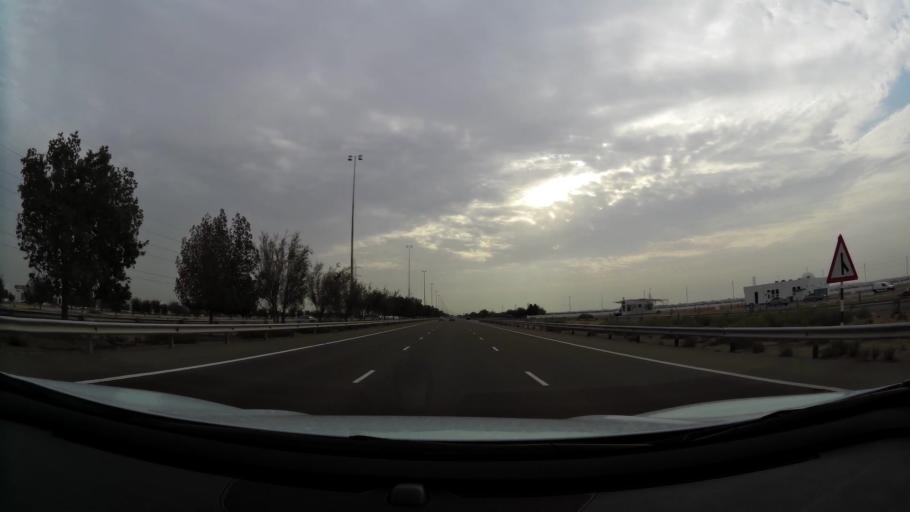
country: AE
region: Abu Dhabi
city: Abu Dhabi
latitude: 24.2184
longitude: 54.8532
